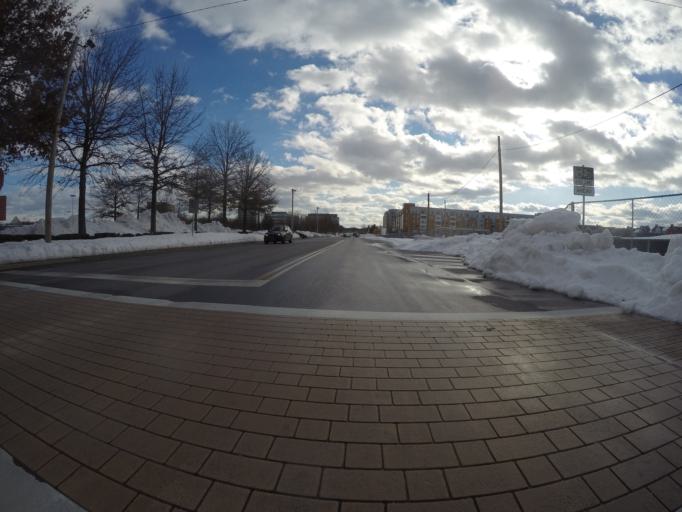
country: US
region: Maryland
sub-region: Howard County
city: Columbia
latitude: 39.2164
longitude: -76.8648
